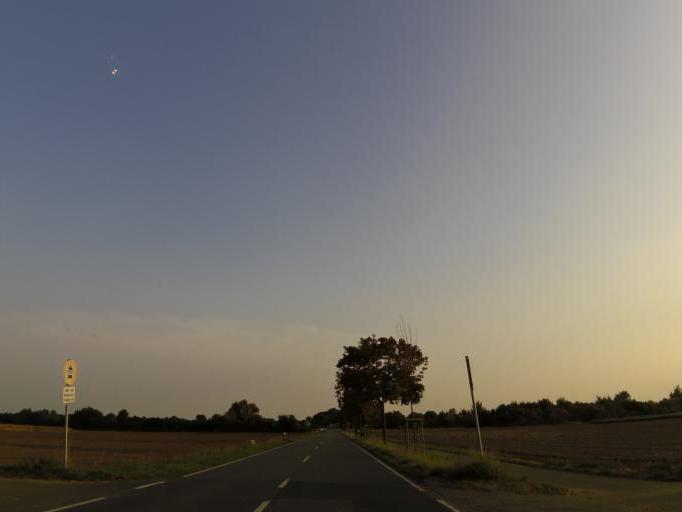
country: DE
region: Hesse
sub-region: Regierungsbezirk Darmstadt
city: Buttelborn
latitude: 49.9137
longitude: 8.5149
